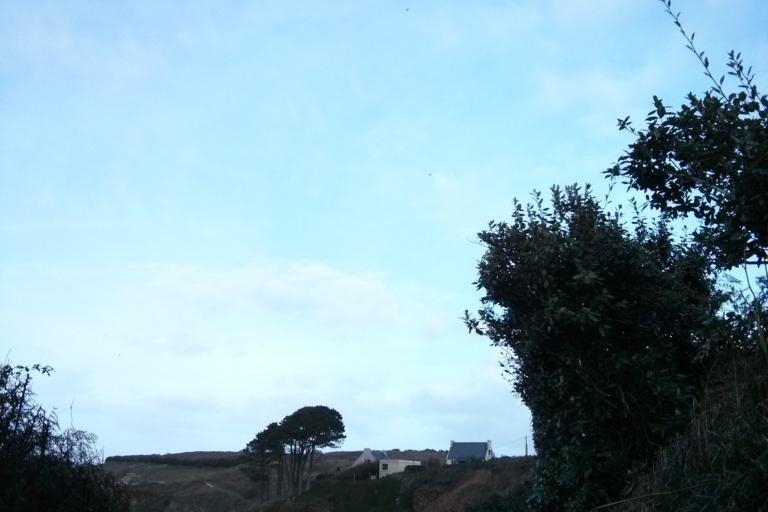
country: FR
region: Brittany
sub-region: Departement du Finistere
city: Le Conquet
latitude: 48.4020
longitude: -4.7742
